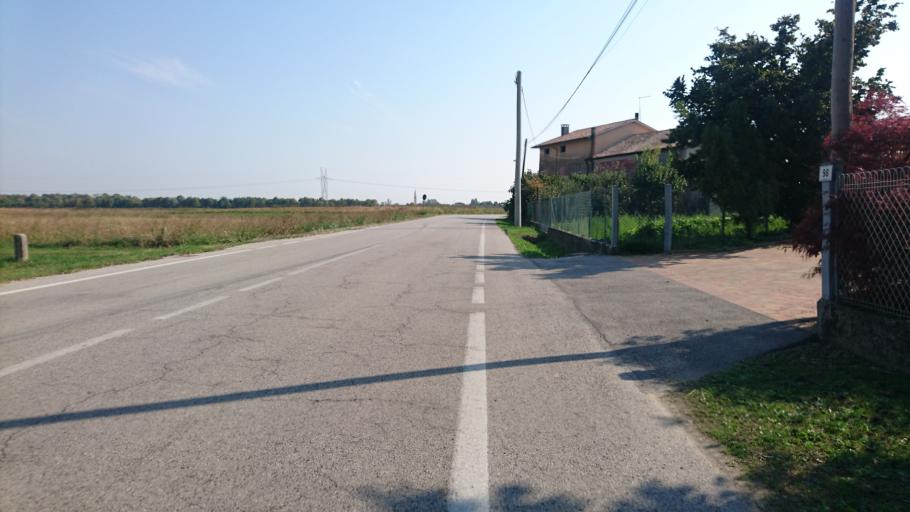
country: IT
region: Veneto
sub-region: Provincia di Vicenza
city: Grumolo delle Abbadesse
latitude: 45.5414
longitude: 11.6717
